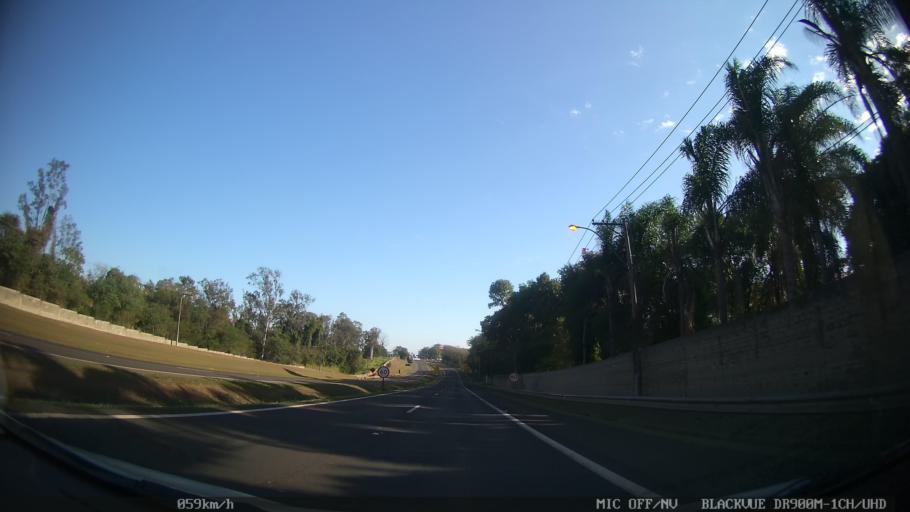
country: BR
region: Sao Paulo
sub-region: Piracicaba
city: Piracicaba
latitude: -22.6954
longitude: -47.6506
